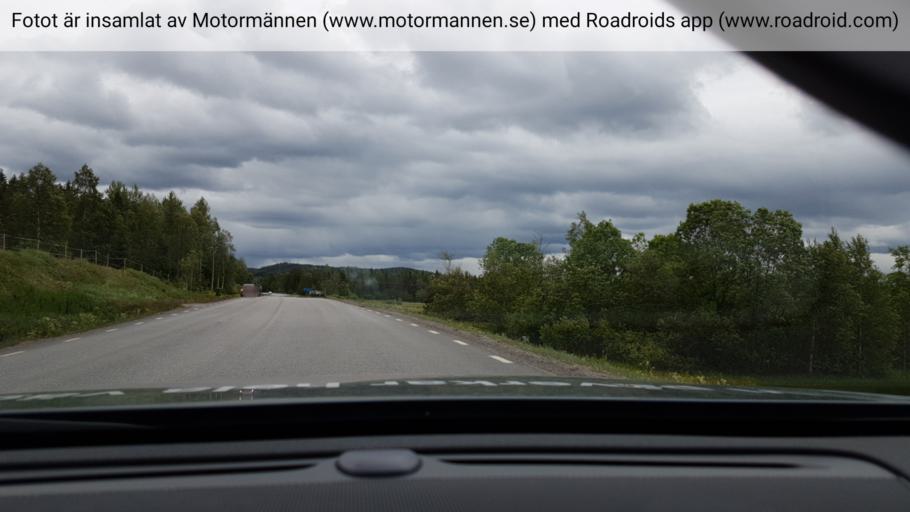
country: SE
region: Vaesterbotten
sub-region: Vannas Kommun
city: Vaennaes
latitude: 63.9277
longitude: 19.7741
